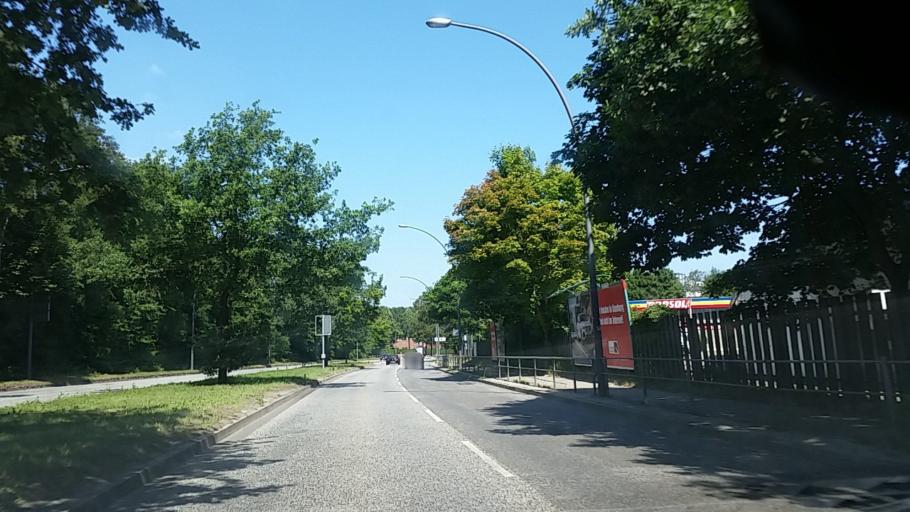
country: DE
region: Hamburg
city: Eidelstedt
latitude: 53.5861
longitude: 9.9061
